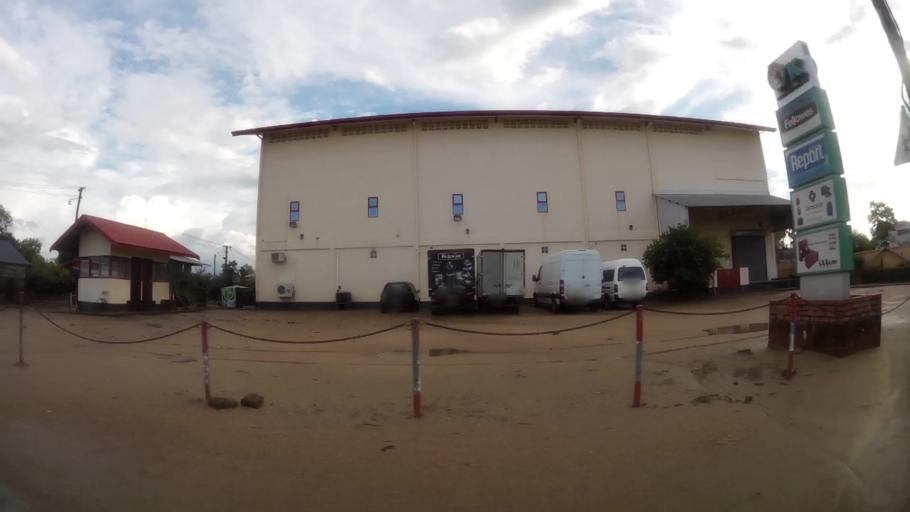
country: SR
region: Paramaribo
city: Paramaribo
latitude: 5.8238
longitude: -55.1808
